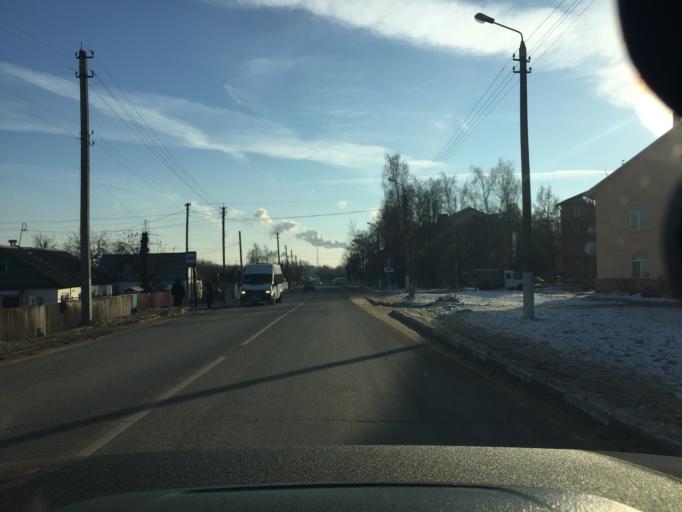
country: RU
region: Tula
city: Tula
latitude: 54.1813
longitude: 37.7099
